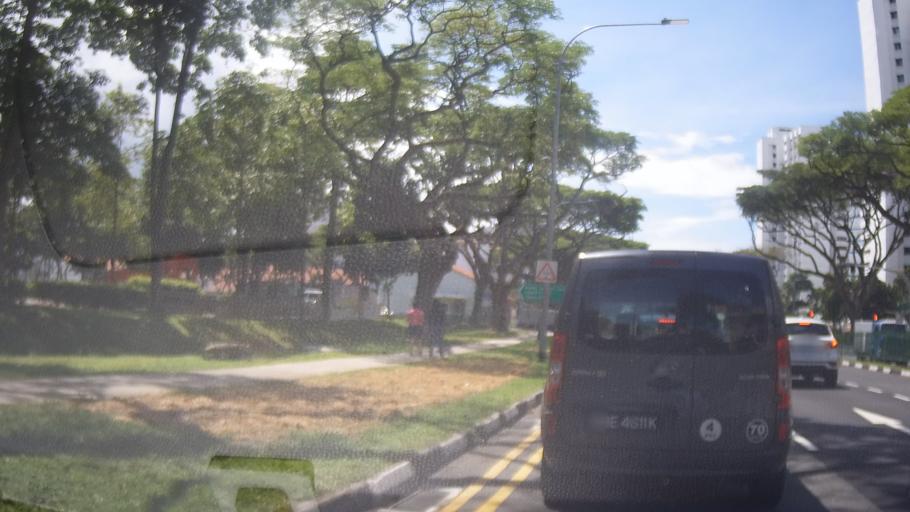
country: SG
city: Singapore
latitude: 1.3187
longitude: 103.8852
